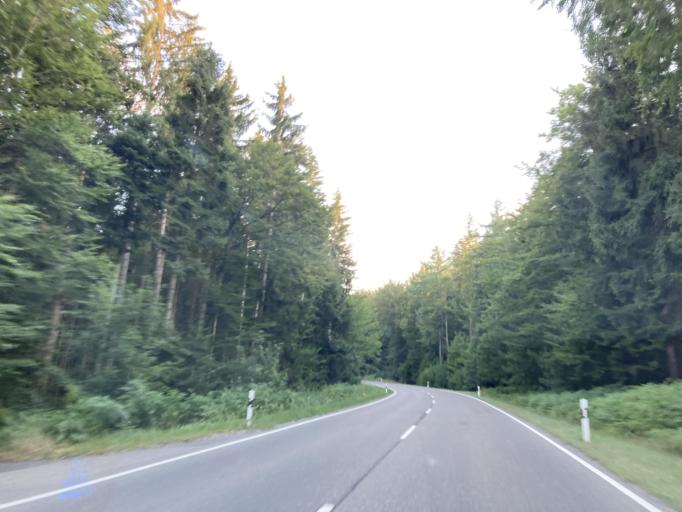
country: DE
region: Baden-Wuerttemberg
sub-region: Karlsruhe Region
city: Dornstetten
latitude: 48.5016
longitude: 8.5129
